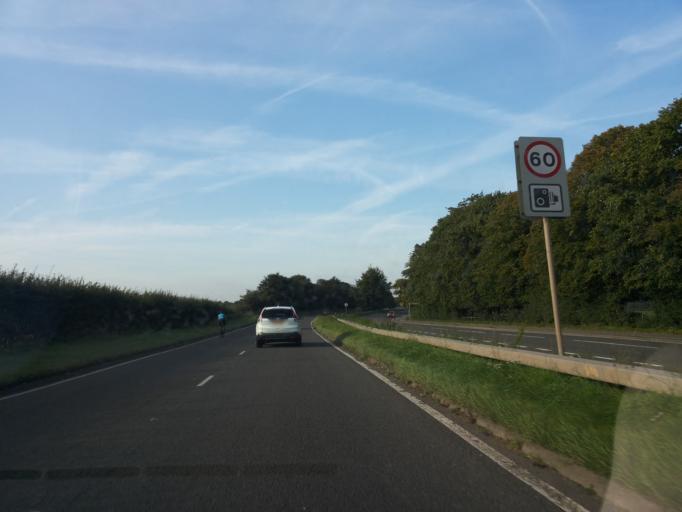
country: GB
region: England
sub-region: Staffordshire
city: Stone
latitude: 52.8797
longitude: -2.1329
